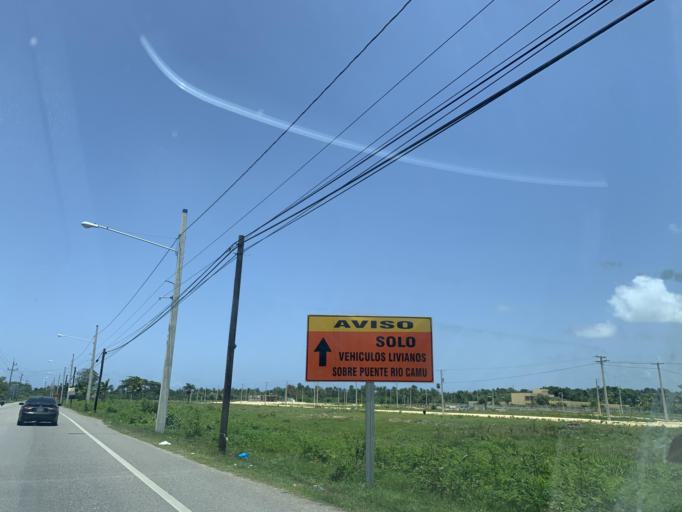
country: DO
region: Puerto Plata
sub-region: Puerto Plata
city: Puerto Plata
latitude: 19.7411
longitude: -70.6015
